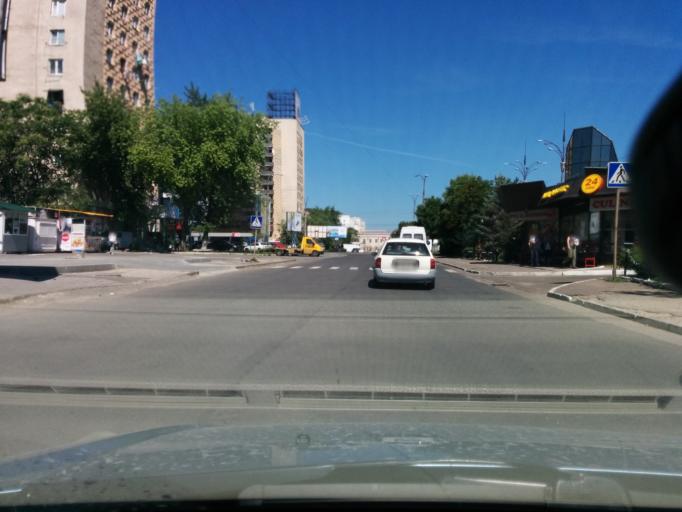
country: MD
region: Chisinau
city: Chisinau
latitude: 47.0327
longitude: 28.8468
